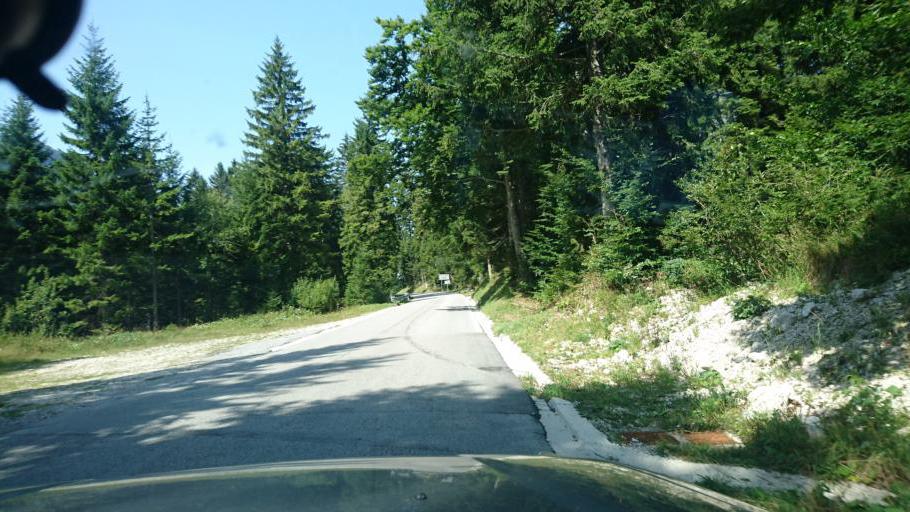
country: SI
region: Bovec
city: Bovec
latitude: 46.3898
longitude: 13.4791
